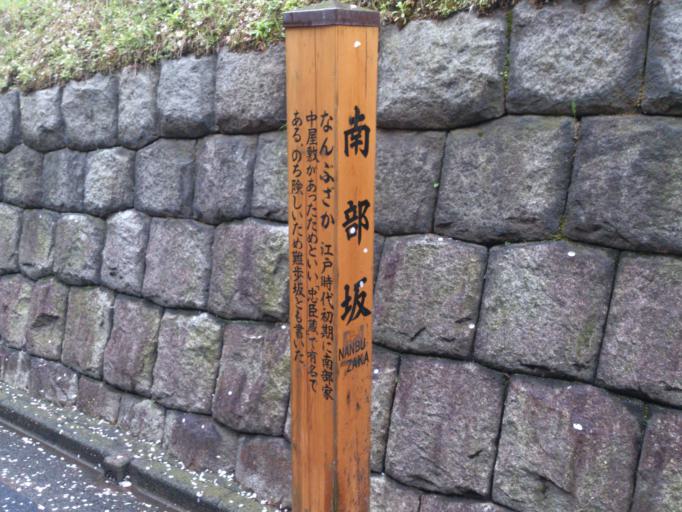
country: JP
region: Tokyo
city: Tokyo
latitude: 35.6684
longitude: 139.7383
